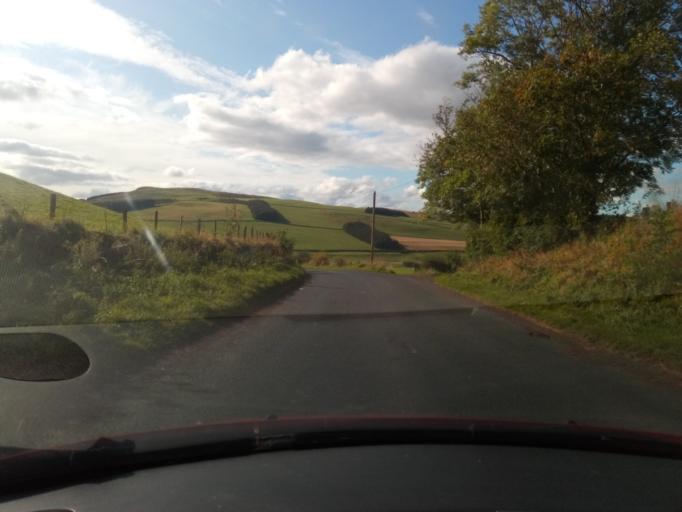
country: GB
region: Scotland
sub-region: The Scottish Borders
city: Coldstream
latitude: 55.5324
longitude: -2.3009
